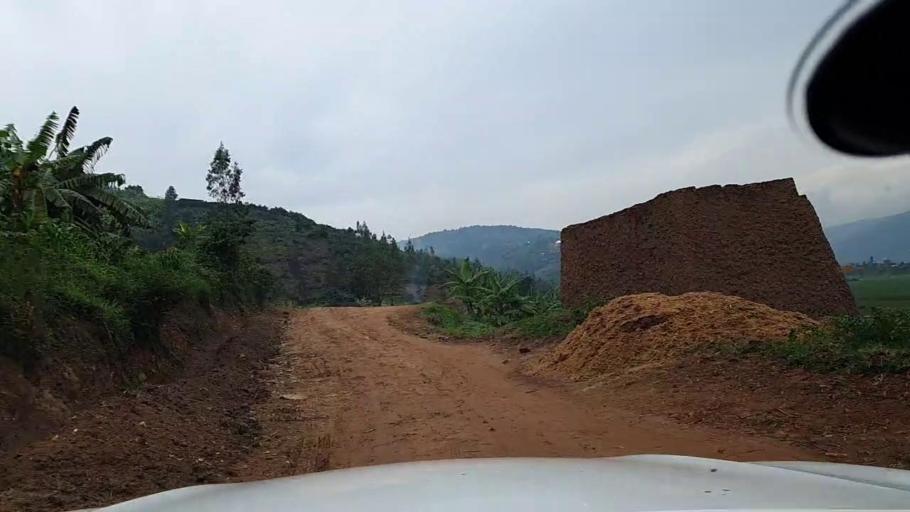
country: RW
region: Kigali
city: Kigali
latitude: -1.9531
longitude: 29.9921
